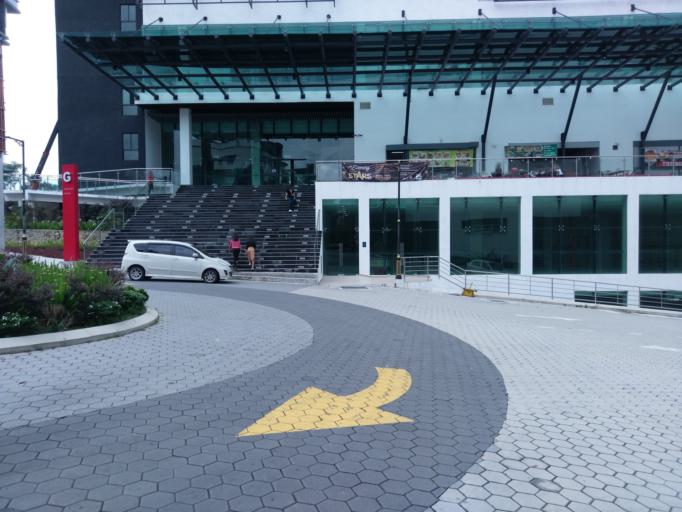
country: MY
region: Selangor
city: Kampong Baharu Balakong
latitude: 3.0784
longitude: 101.7331
